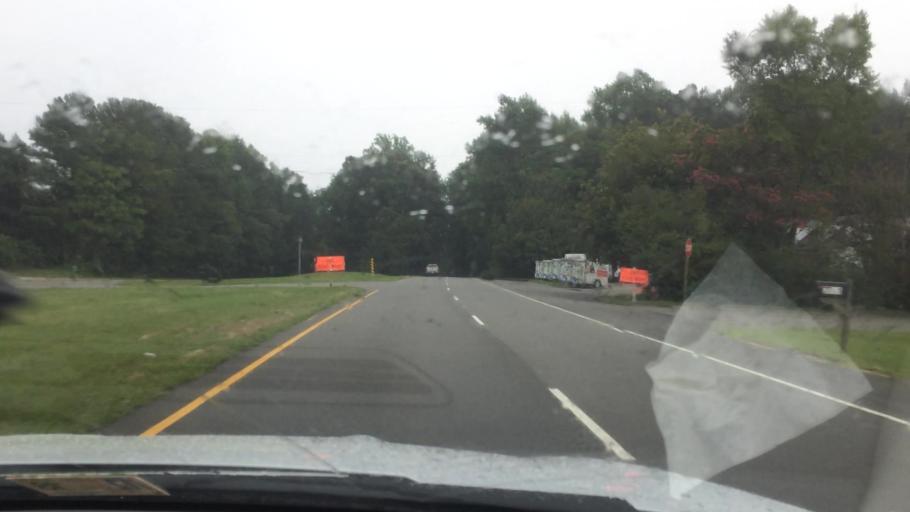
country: US
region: Virginia
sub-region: James City County
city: Williamsburg
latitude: 37.3974
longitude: -76.7889
